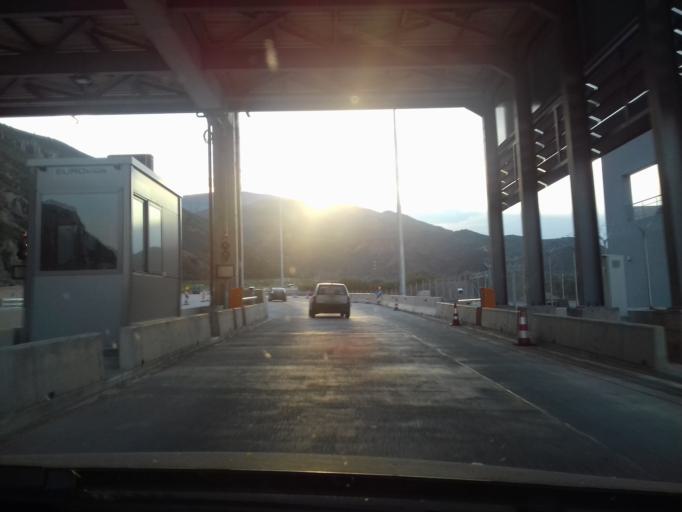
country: GR
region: West Greece
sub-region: Nomos Achaias
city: Temeni
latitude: 38.1911
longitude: 22.1655
